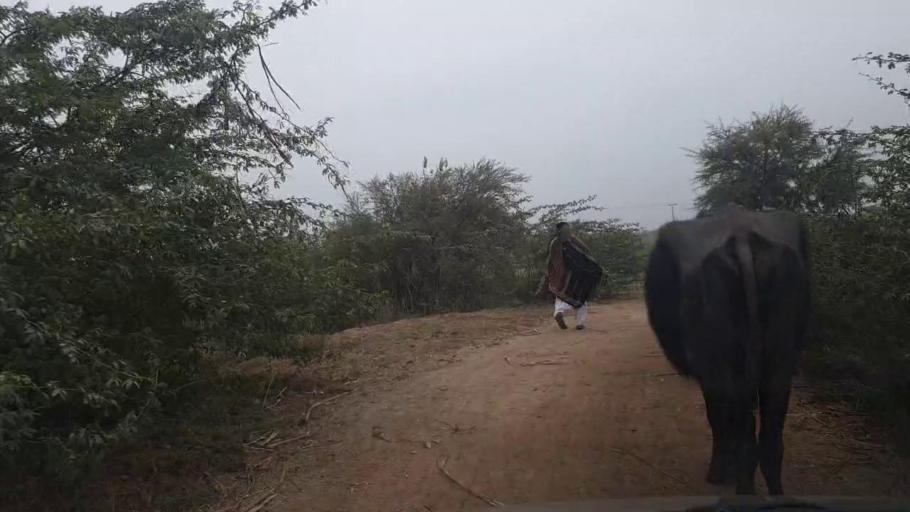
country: PK
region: Sindh
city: Tando Adam
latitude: 25.8371
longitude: 68.7237
